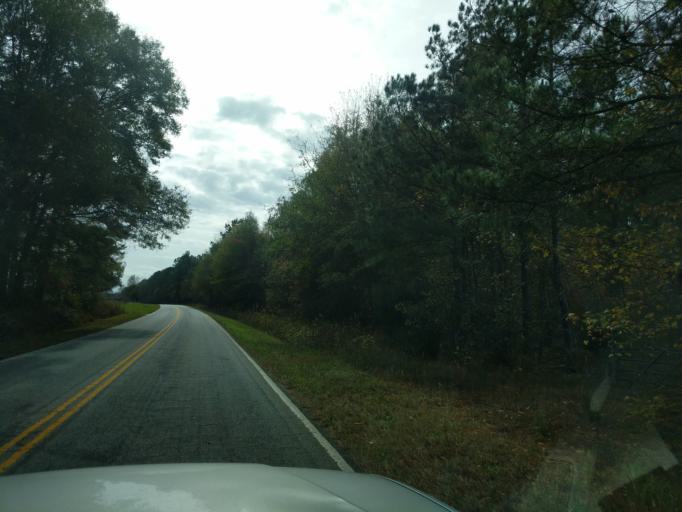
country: US
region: South Carolina
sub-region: Laurens County
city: Joanna
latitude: 34.3600
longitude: -81.8609
